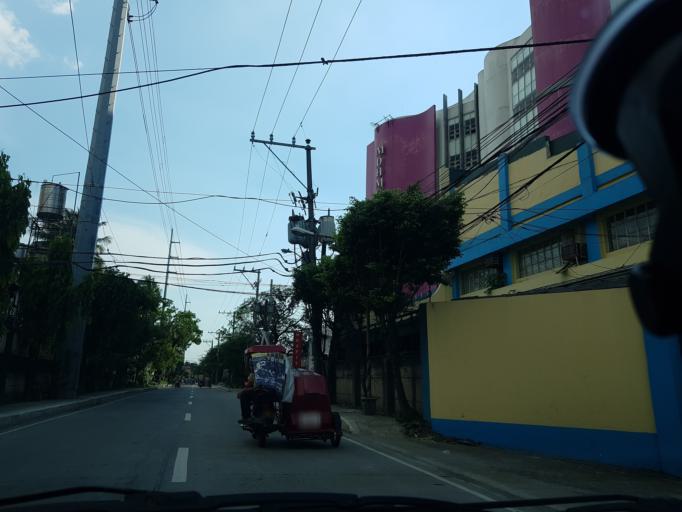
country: PH
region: Metro Manila
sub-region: Marikina
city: Calumpang
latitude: 14.6213
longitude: 121.0831
